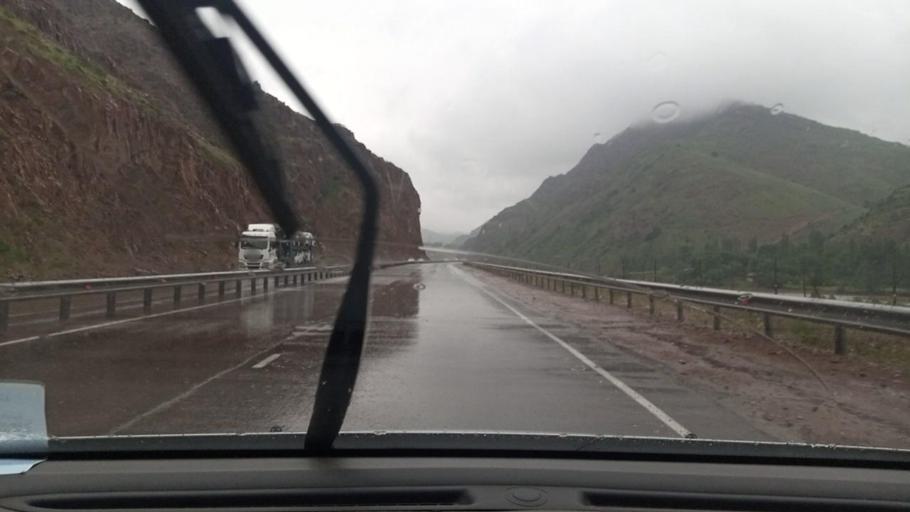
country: UZ
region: Toshkent
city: Angren
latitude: 41.1163
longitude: 70.3423
